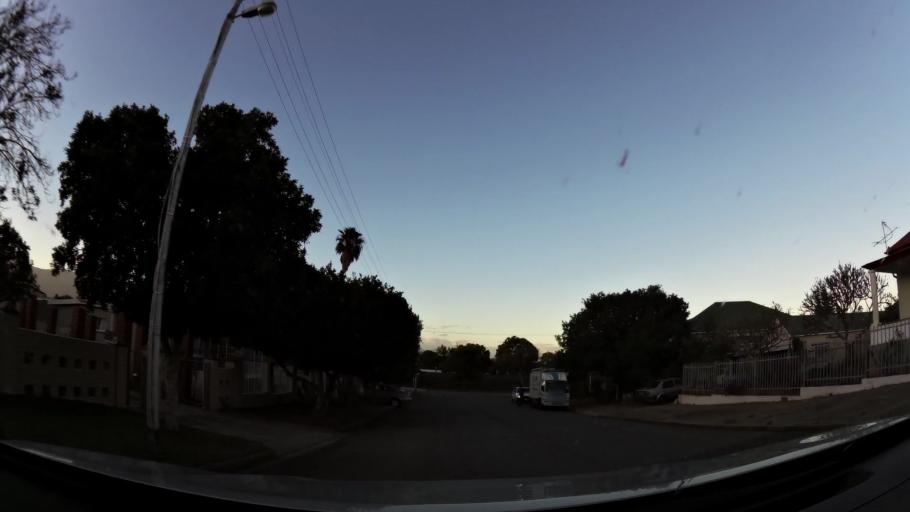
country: ZA
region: Western Cape
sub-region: Eden District Municipality
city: Riversdale
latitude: -34.0903
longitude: 21.2536
